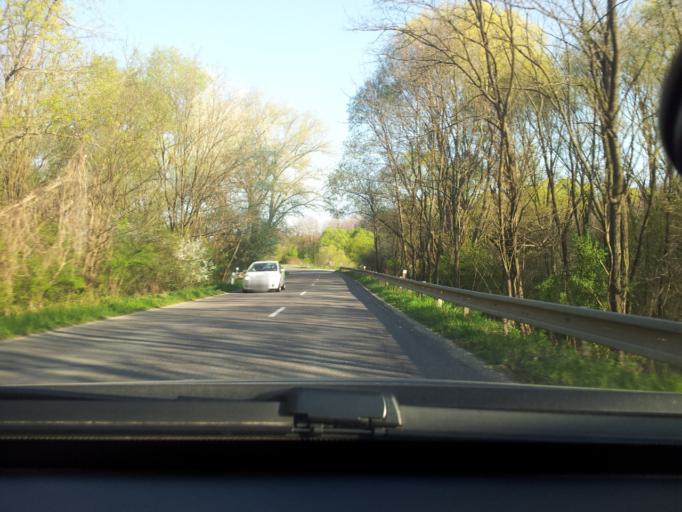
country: SK
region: Nitriansky
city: Tlmace
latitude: 48.3016
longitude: 18.4497
